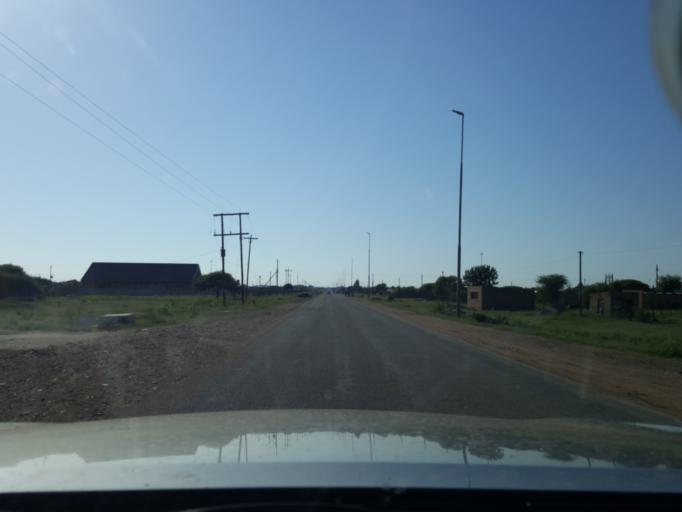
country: ZA
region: North-West
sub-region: Ngaka Modiri Molema District Municipality
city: Mmabatho
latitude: -25.8319
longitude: 25.6574
